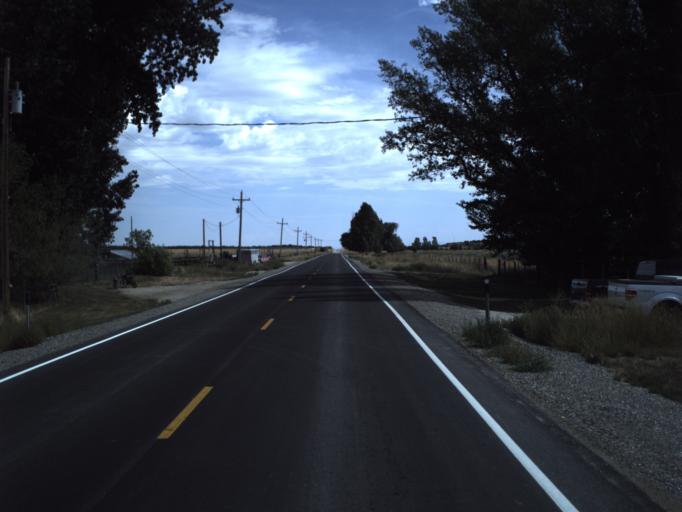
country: US
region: Idaho
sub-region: Cassia County
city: Burley
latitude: 41.8170
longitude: -113.3187
